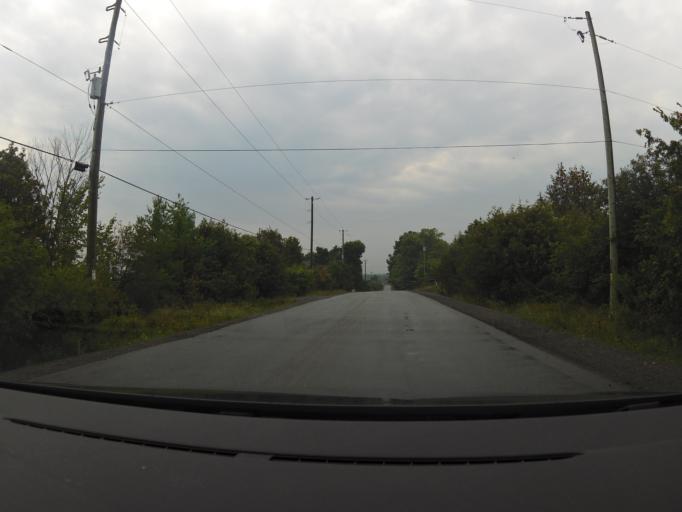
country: CA
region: Ontario
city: Carleton Place
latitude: 45.2024
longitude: -76.0576
